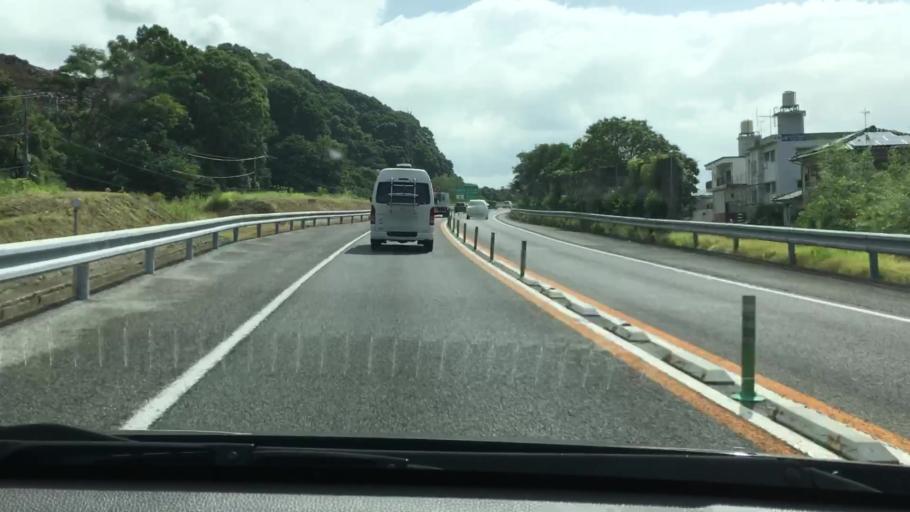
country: JP
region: Nagasaki
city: Sasebo
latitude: 33.1518
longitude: 129.7613
